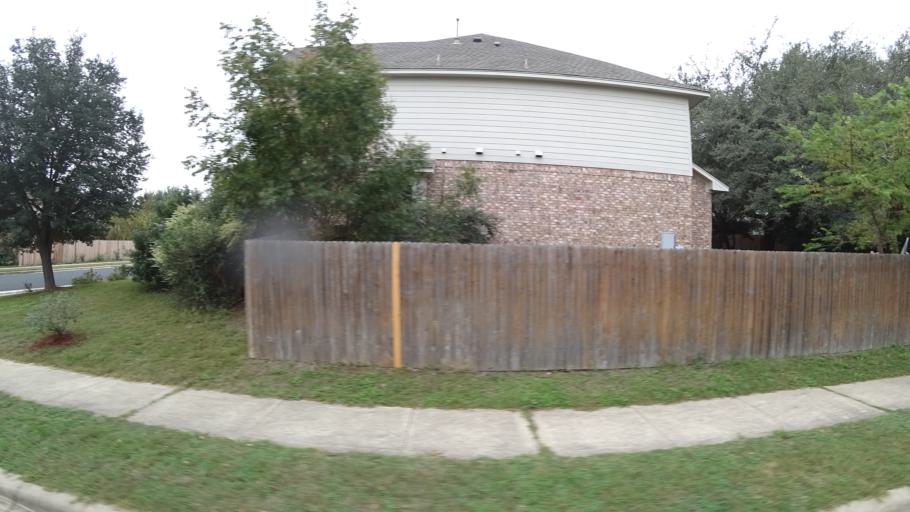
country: US
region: Texas
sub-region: Williamson County
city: Anderson Mill
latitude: 30.4328
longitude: -97.8179
